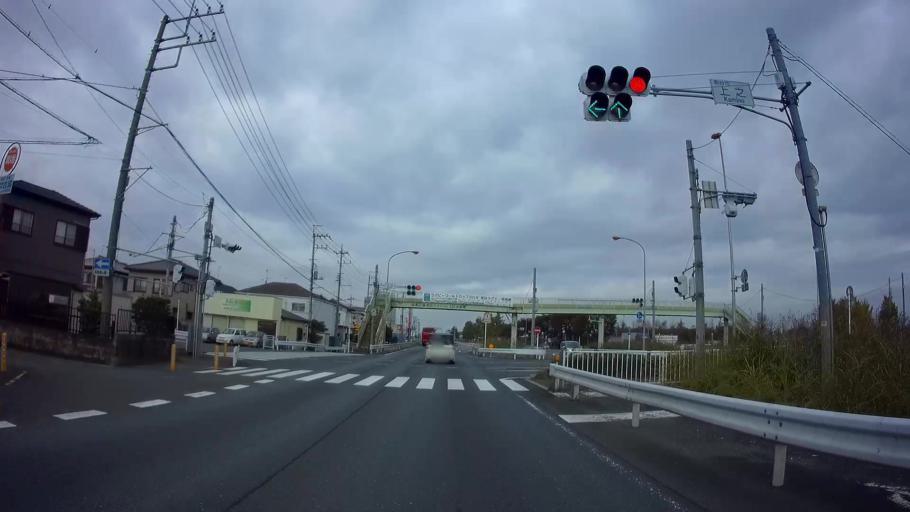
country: JP
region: Saitama
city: Kumagaya
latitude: 36.1571
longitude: 139.4090
